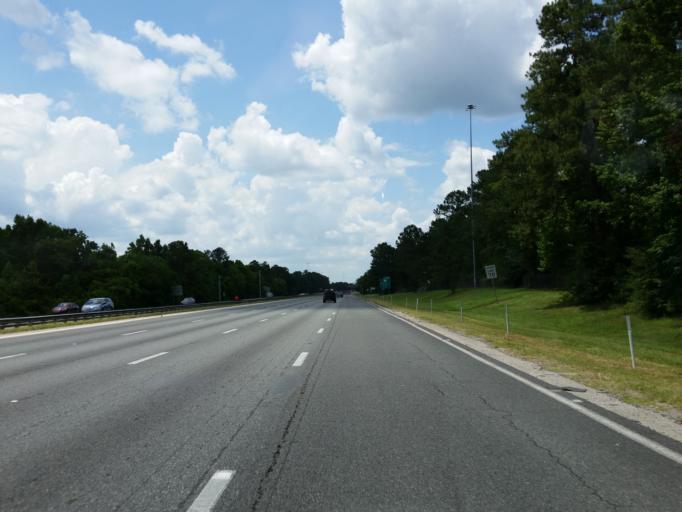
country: US
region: Florida
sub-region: Alachua County
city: Gainesville
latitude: 29.6065
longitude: -82.3770
